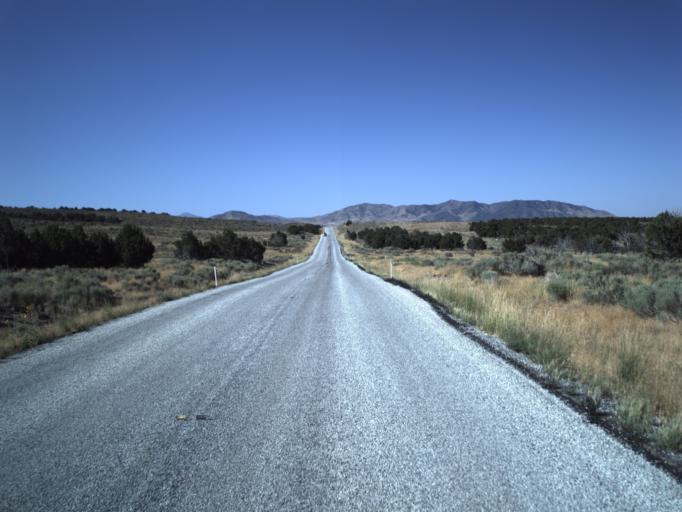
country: US
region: Utah
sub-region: Juab County
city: Mona
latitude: 39.7892
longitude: -112.1493
